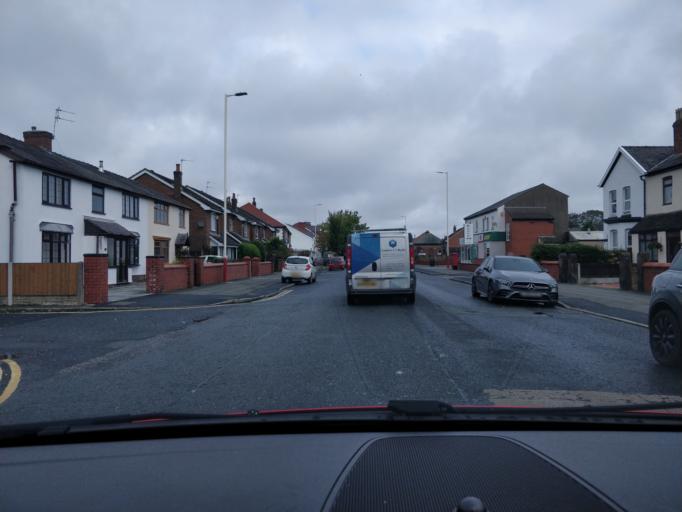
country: GB
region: England
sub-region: Sefton
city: Southport
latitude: 53.6183
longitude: -3.0159
